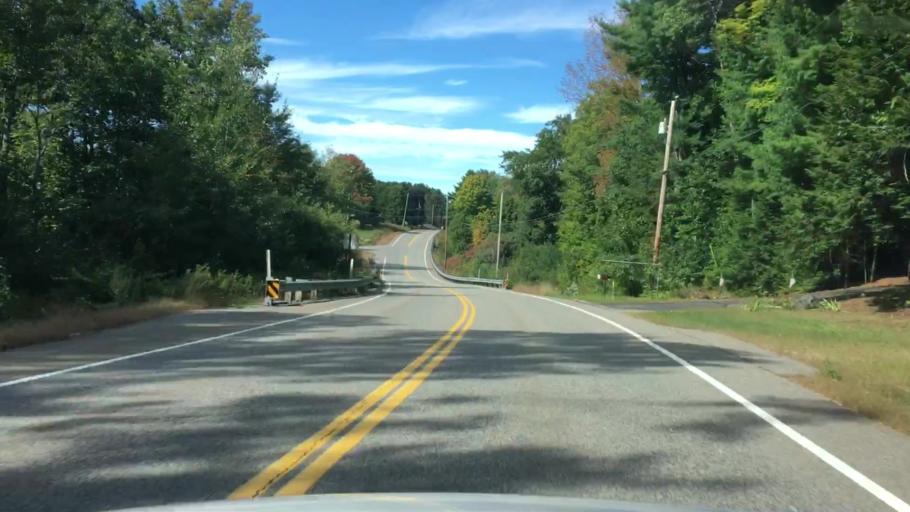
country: US
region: Maine
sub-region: Cumberland County
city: Westbrook
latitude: 43.6555
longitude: -70.4001
